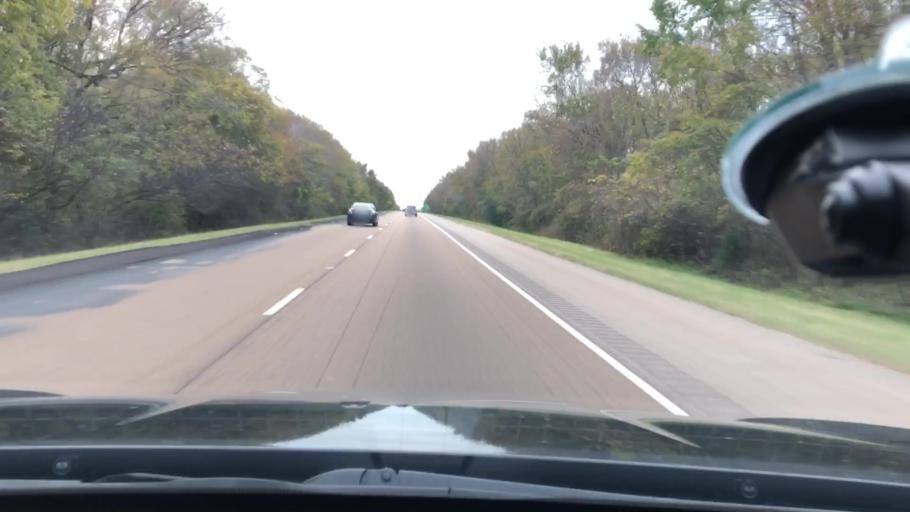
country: US
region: Arkansas
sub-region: Nevada County
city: Prescott
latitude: 33.8031
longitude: -93.4333
